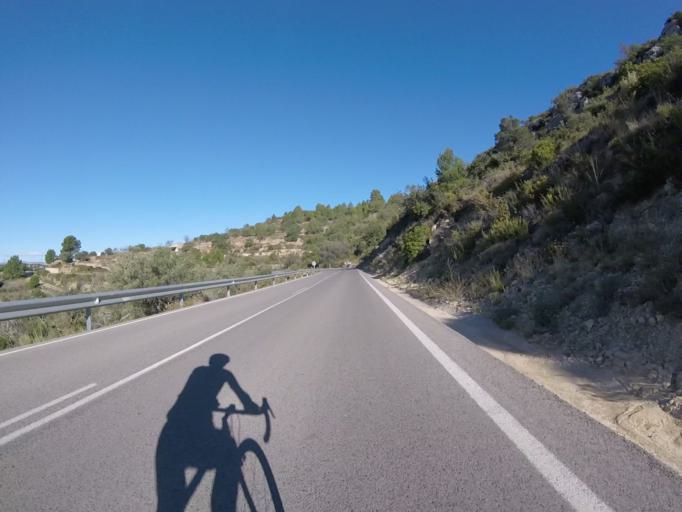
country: ES
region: Valencia
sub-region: Provincia de Castello
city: Cervera del Maestre
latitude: 40.4575
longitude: 0.2656
